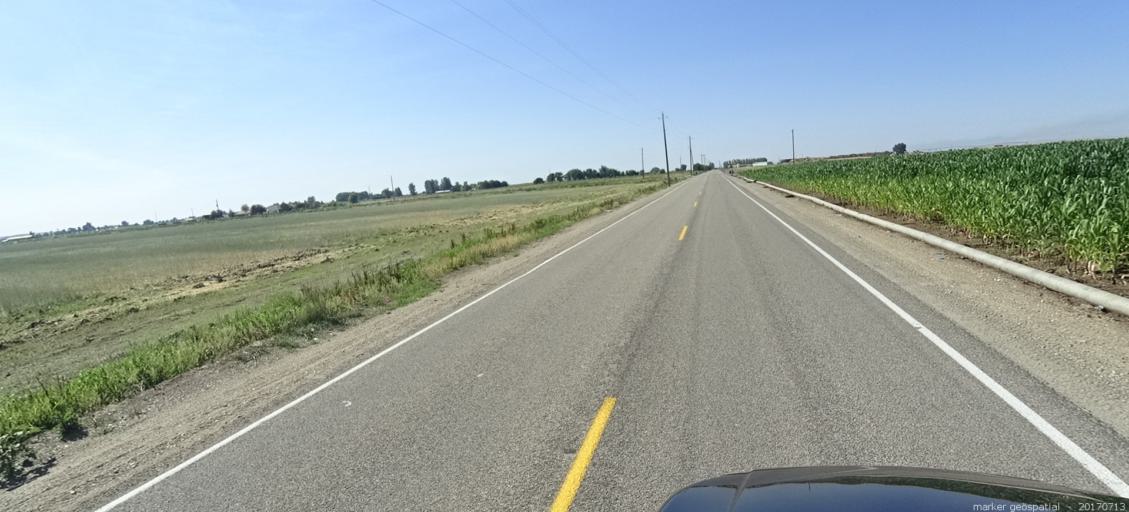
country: US
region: Idaho
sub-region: Ada County
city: Kuna
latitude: 43.5407
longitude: -116.3744
